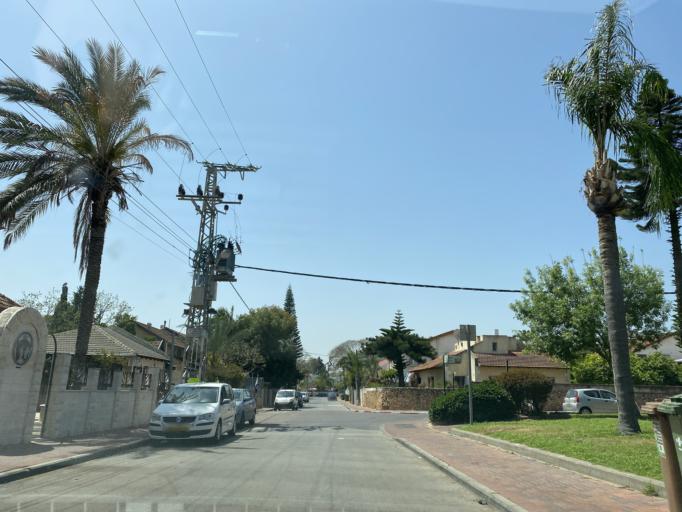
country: IL
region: Central District
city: Ra'anana
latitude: 32.1918
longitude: 34.8687
